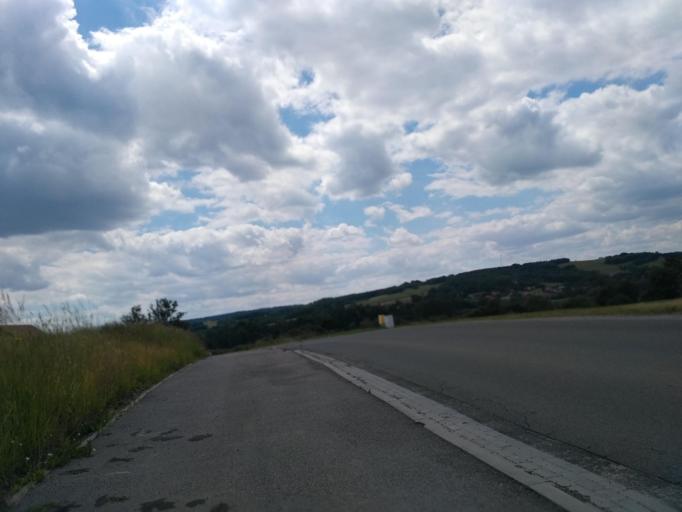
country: PL
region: Subcarpathian Voivodeship
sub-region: Powiat brzozowski
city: Nozdrzec
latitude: 49.7755
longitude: 22.2230
